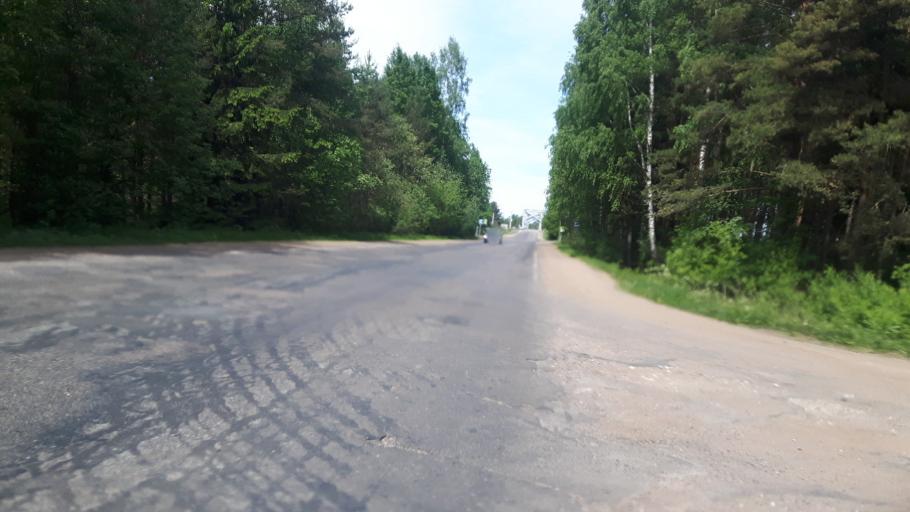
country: RU
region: Leningrad
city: Ust'-Luga
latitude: 59.6495
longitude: 28.2619
